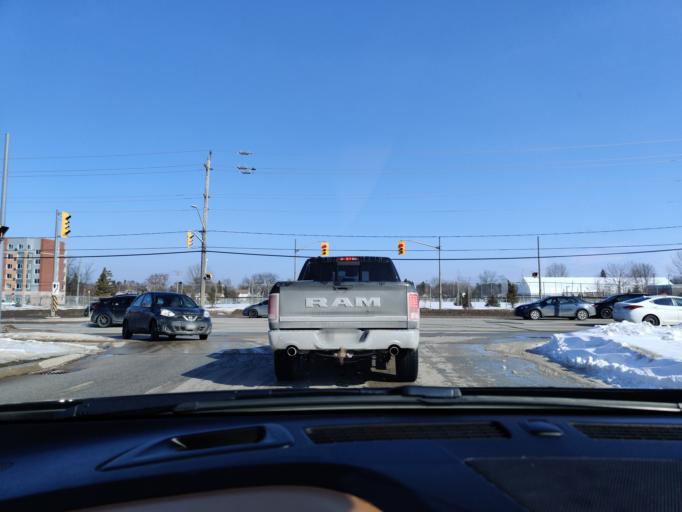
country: CA
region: Ontario
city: Collingwood
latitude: 44.4984
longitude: -80.2342
